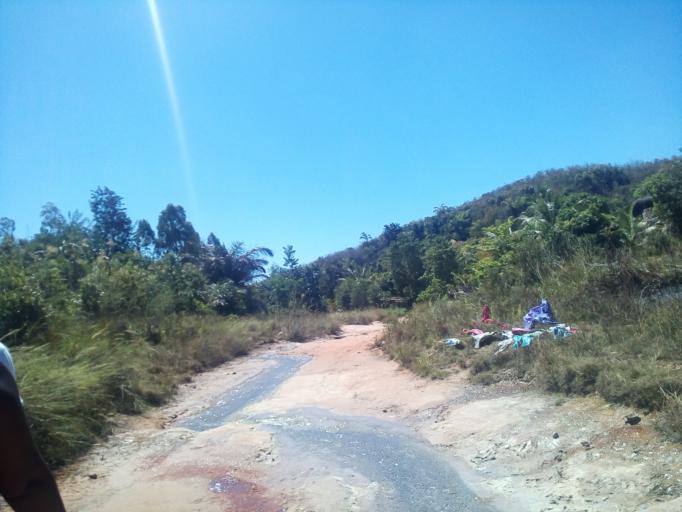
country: MG
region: Boeny
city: Mahajanga
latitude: -15.6320
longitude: 46.3507
